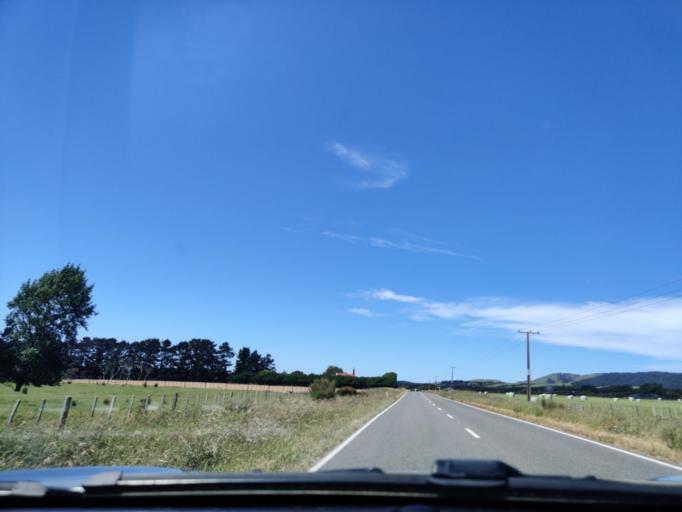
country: NZ
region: Wellington
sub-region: Upper Hutt City
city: Upper Hutt
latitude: -41.3291
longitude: 175.2370
